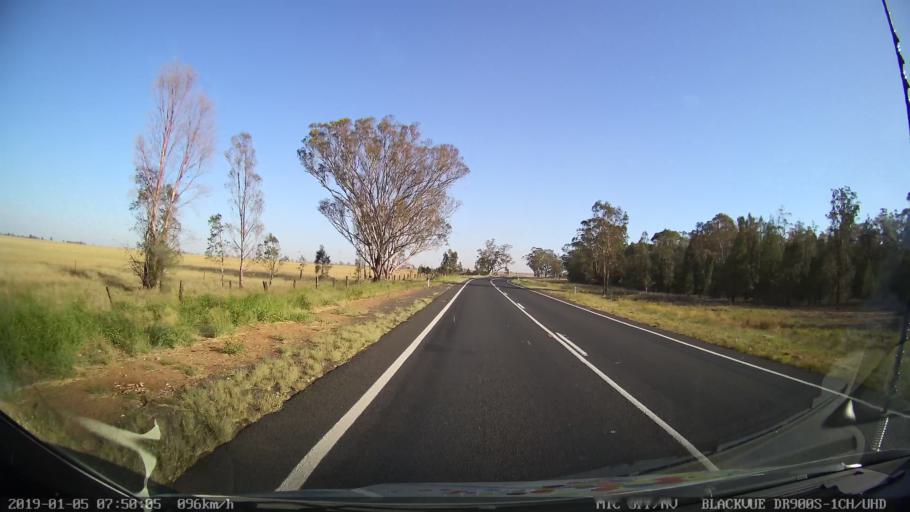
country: AU
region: New South Wales
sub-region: Gilgandra
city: Gilgandra
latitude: -31.7924
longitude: 148.6357
